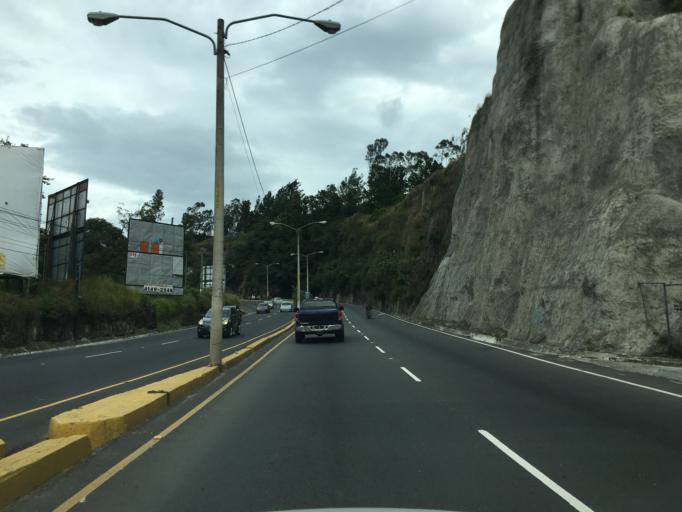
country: GT
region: Guatemala
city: Mixco
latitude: 14.5926
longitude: -90.5726
